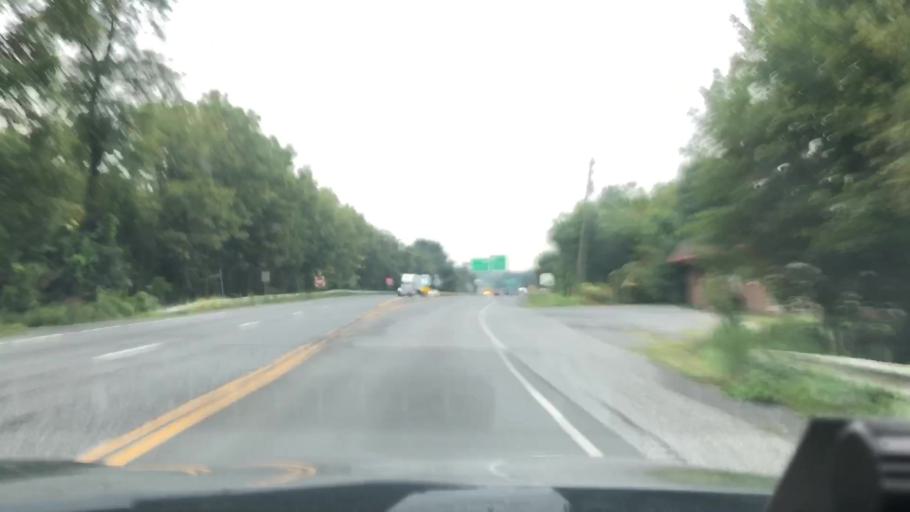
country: US
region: Pennsylvania
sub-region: Berks County
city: Blandon
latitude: 40.4396
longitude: -75.9069
